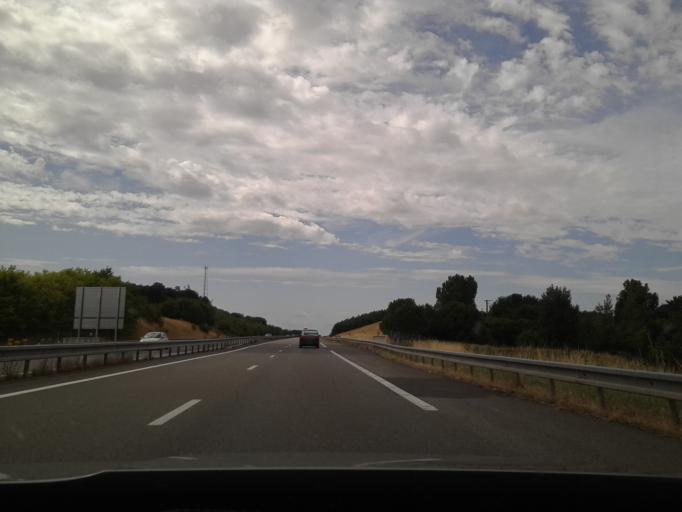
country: FR
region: Pays de la Loire
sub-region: Departement de la Sarthe
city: Sainte-Jamme-sur-Sarthe
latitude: 48.1517
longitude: 0.1431
